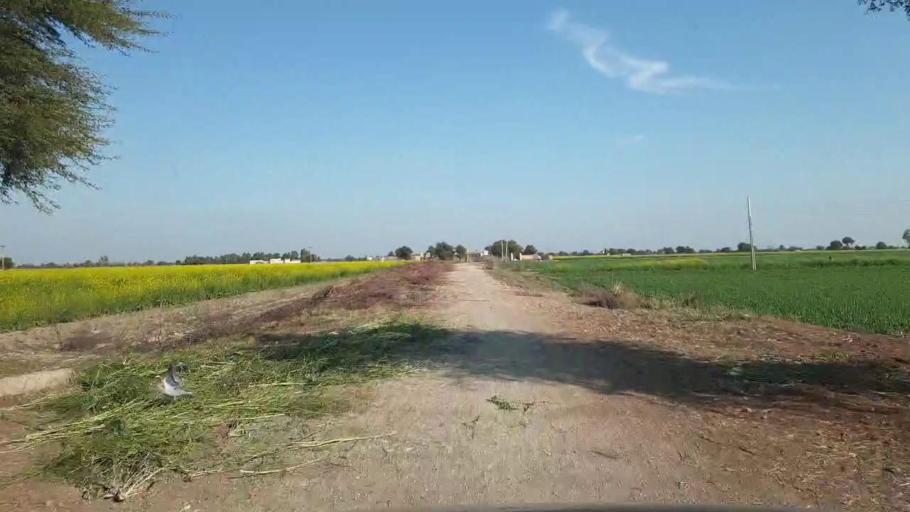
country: PK
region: Sindh
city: Shahpur Chakar
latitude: 26.1757
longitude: 68.6679
